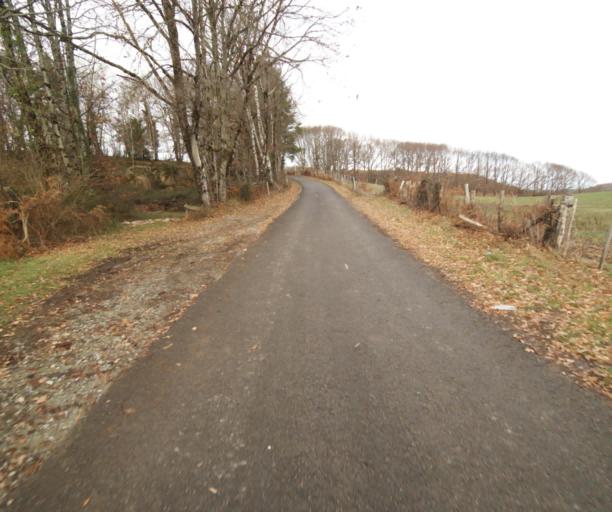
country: FR
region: Limousin
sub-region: Departement de la Correze
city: Saint-Mexant
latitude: 45.2776
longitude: 1.6500
